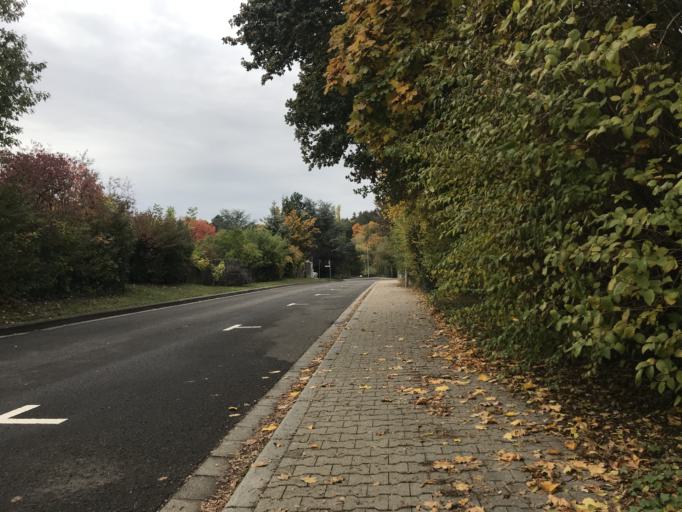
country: DE
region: Rheinland-Pfalz
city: Kirchheimbolanden
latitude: 49.6577
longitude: 8.0056
